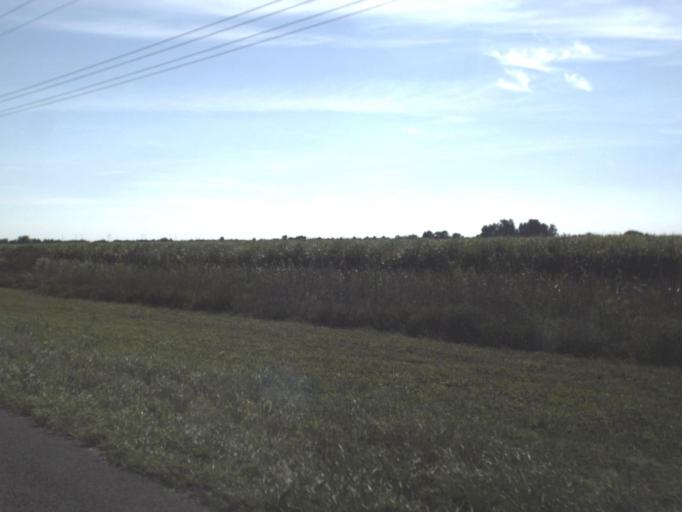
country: US
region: Florida
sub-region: Glades County
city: Moore Haven
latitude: 26.7822
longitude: -81.0830
